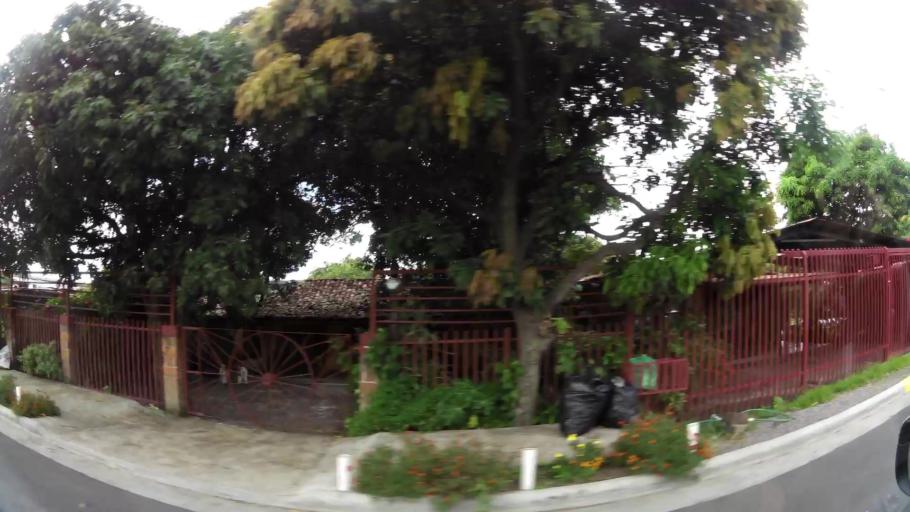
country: CR
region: San Jose
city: Santa Ana
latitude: 9.9315
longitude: -84.1840
